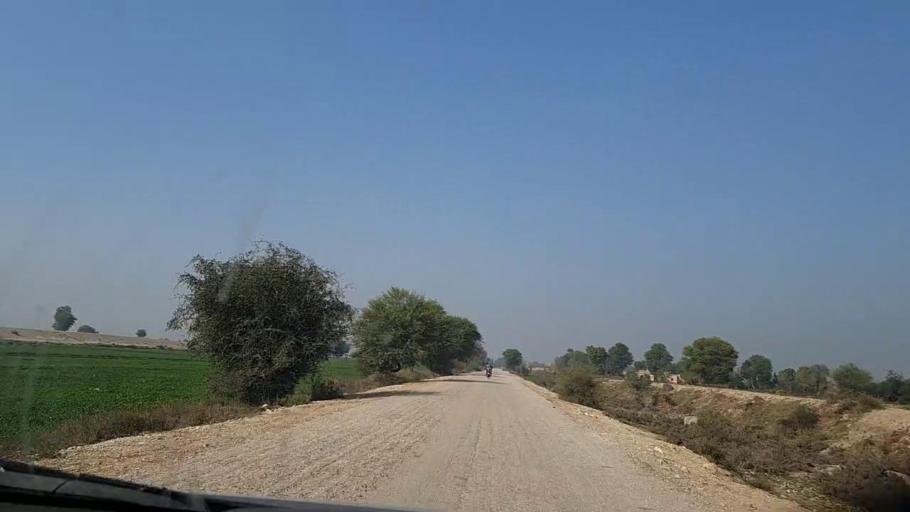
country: PK
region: Sindh
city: Moro
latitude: 26.7330
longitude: 67.9202
